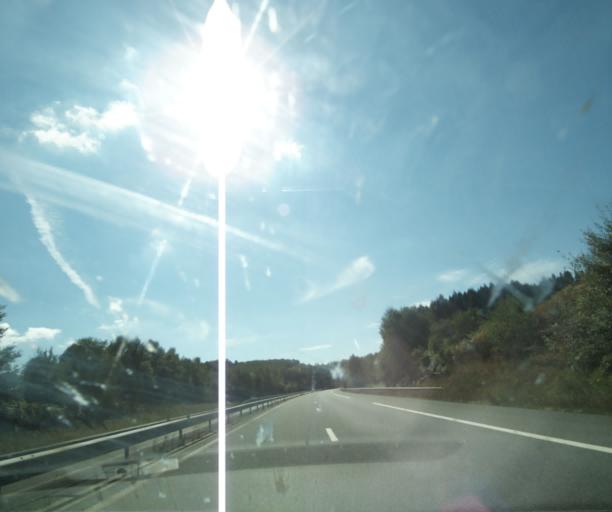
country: FR
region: Limousin
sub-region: Departement de la Correze
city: Egletons
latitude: 45.3762
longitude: 1.9672
